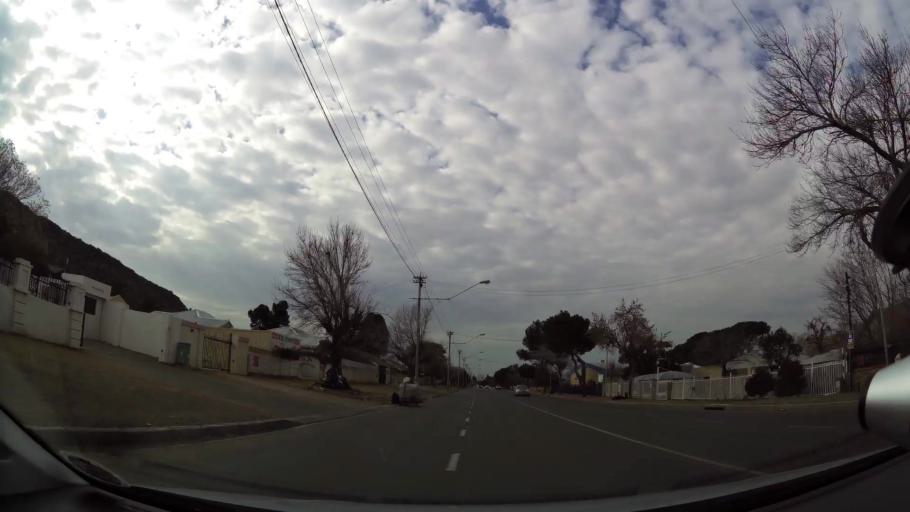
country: ZA
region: Orange Free State
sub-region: Mangaung Metropolitan Municipality
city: Bloemfontein
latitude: -29.1006
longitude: 26.2420
